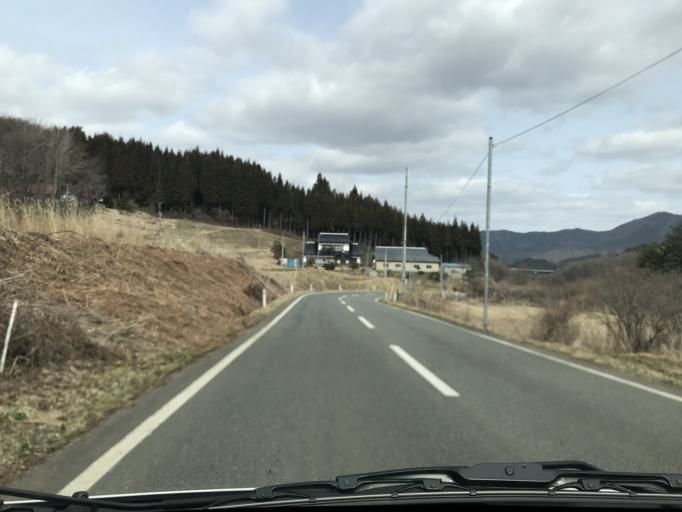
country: JP
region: Iwate
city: Kitakami
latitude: 39.2749
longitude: 141.3197
